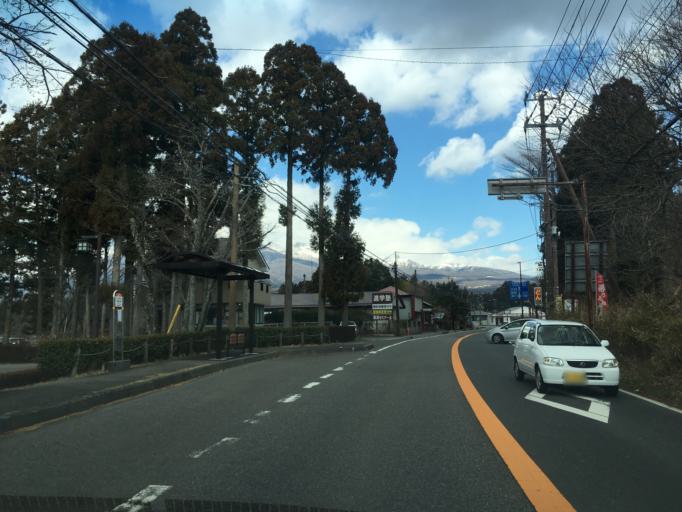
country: JP
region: Tochigi
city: Kuroiso
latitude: 37.0416
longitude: 140.0143
